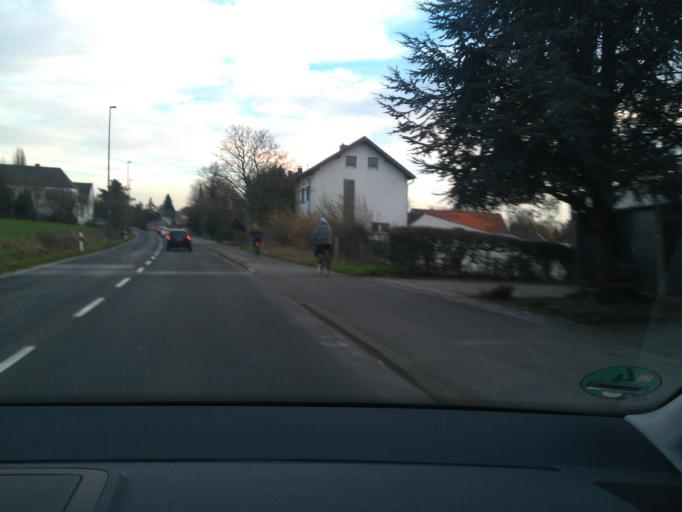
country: DE
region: North Rhine-Westphalia
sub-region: Regierungsbezirk Koln
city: Aachen
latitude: 50.7373
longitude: 6.1297
